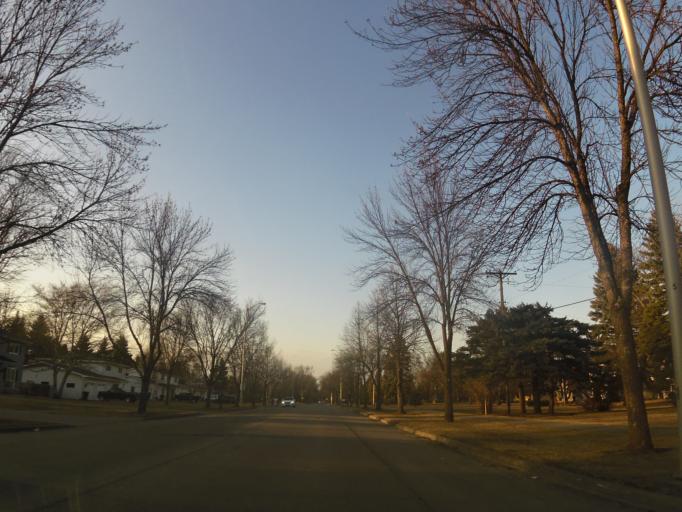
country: US
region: North Dakota
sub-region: Grand Forks County
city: Grand Forks
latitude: 47.8875
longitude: -97.0291
